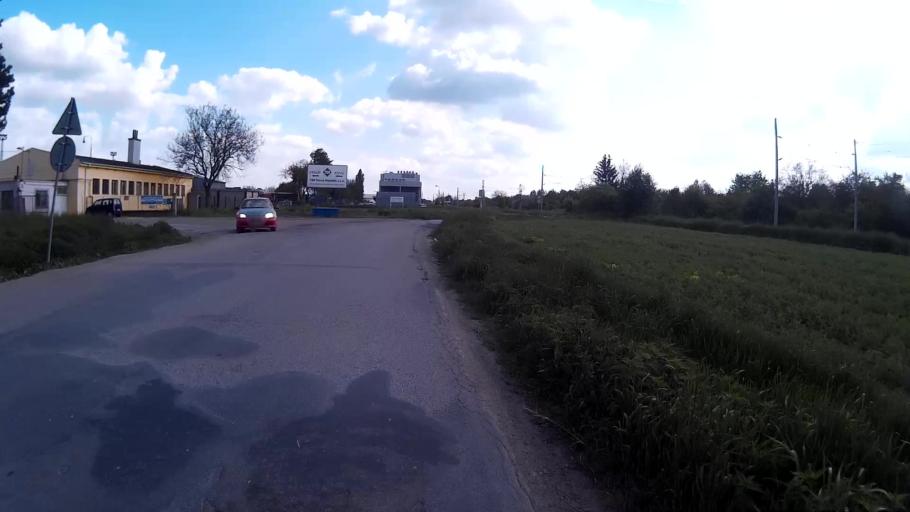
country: CZ
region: South Moravian
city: Modrice
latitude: 49.1187
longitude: 16.6064
